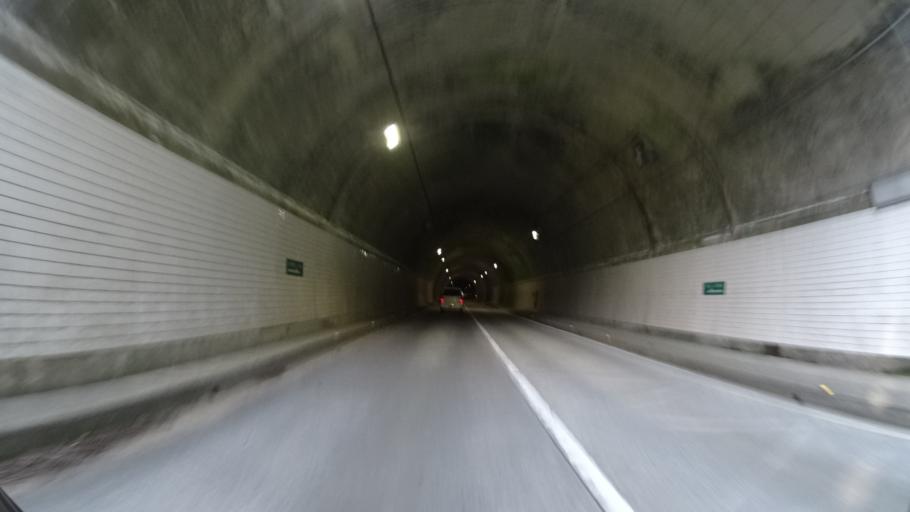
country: JP
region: Ehime
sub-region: Nishiuwa-gun
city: Ikata-cho
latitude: 33.4291
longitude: 132.2112
